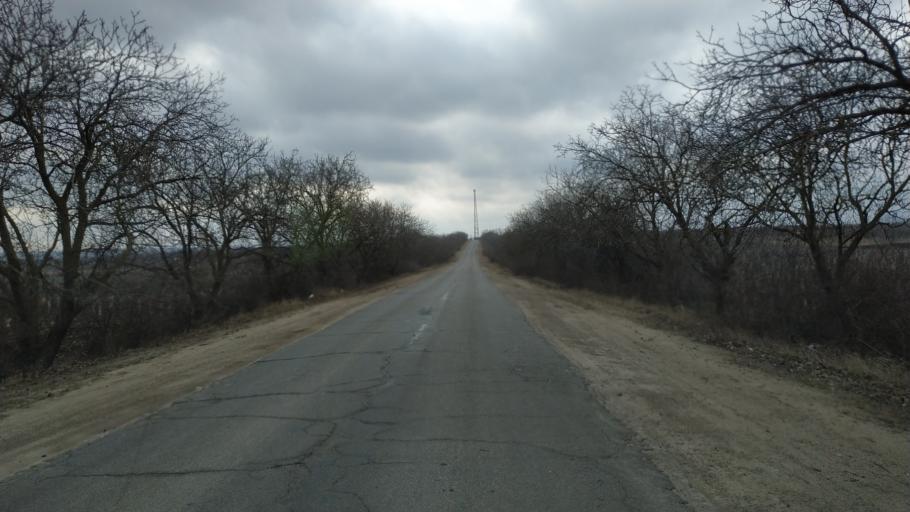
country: MD
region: Laloveni
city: Ialoveni
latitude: 46.8950
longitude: 28.7712
